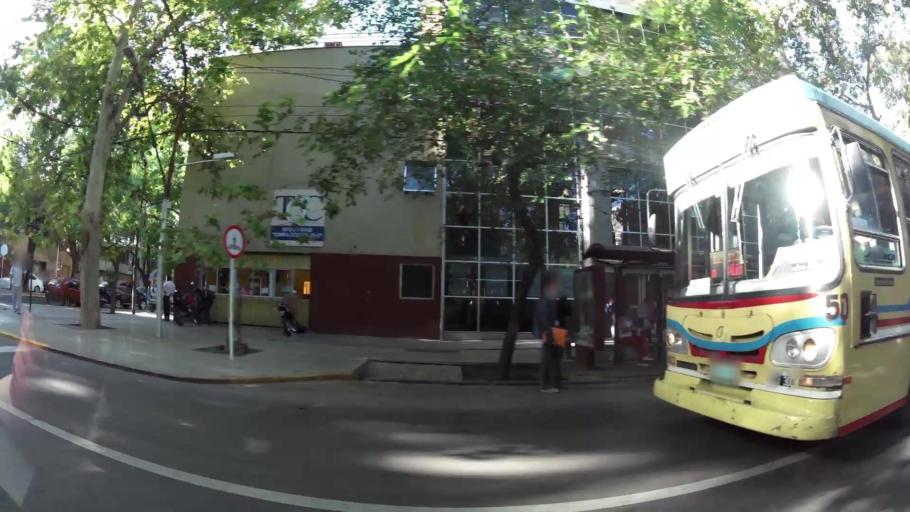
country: AR
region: Mendoza
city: Mendoza
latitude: -32.8919
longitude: -68.8448
